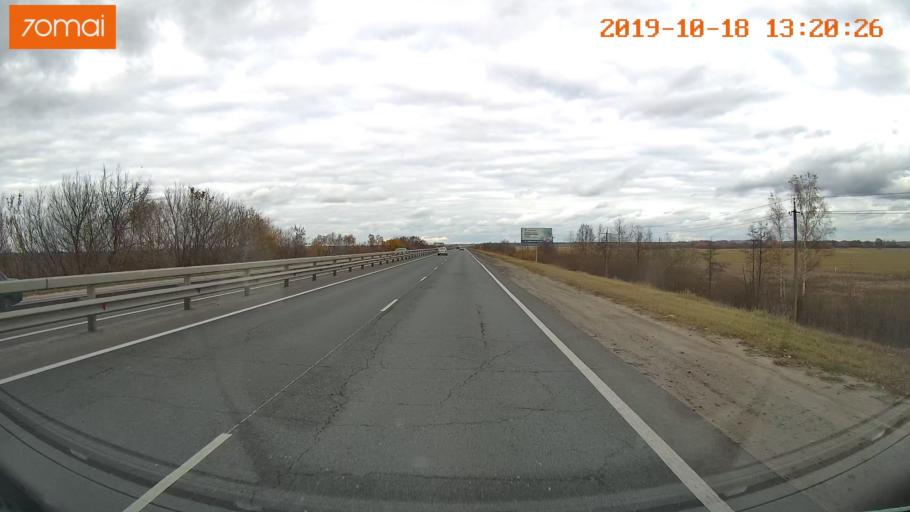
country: RU
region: Rjazan
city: Polyany
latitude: 54.6807
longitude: 39.8319
